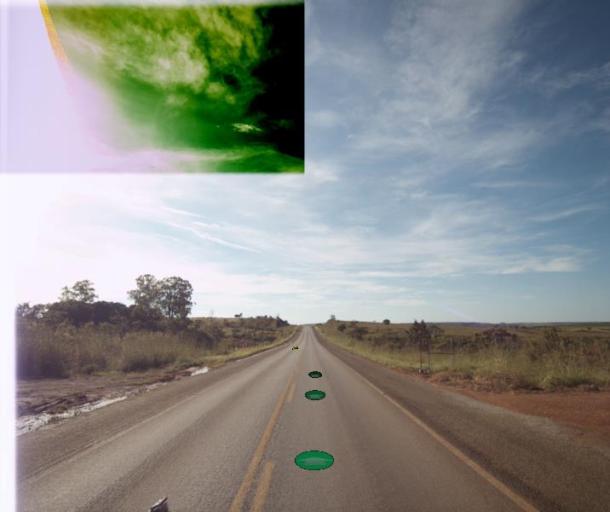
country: BR
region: Goias
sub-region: Abadiania
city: Abadiania
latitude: -15.7831
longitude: -48.4874
